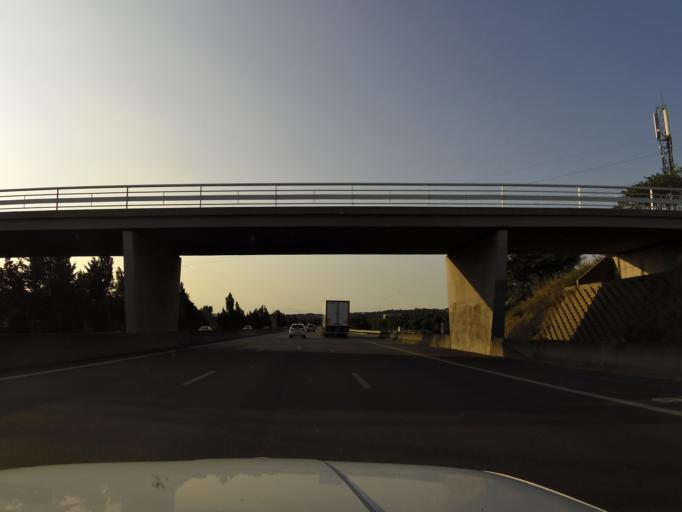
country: FR
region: Rhone-Alpes
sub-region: Departement de l'Isere
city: Salaise-sur-Sanne
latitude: 45.3489
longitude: 4.8065
